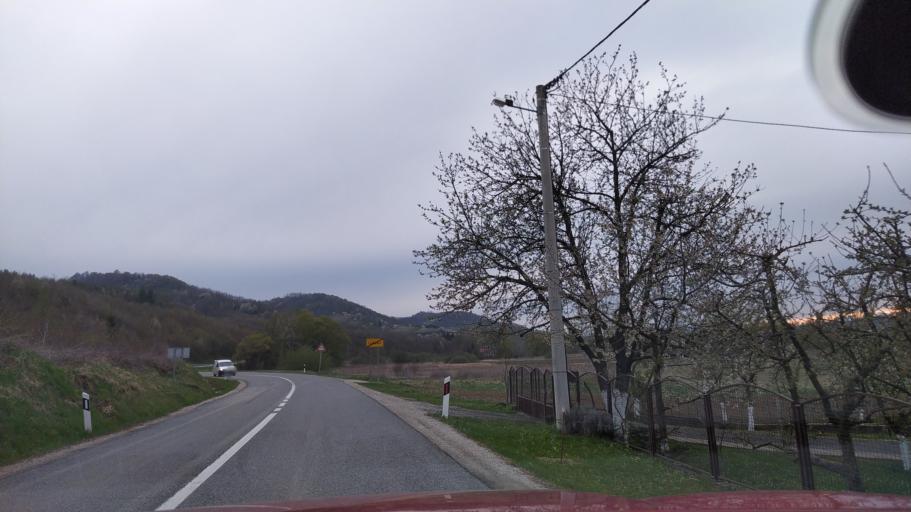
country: HR
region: Varazdinska
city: Jalzabet
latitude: 46.2141
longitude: 16.5073
